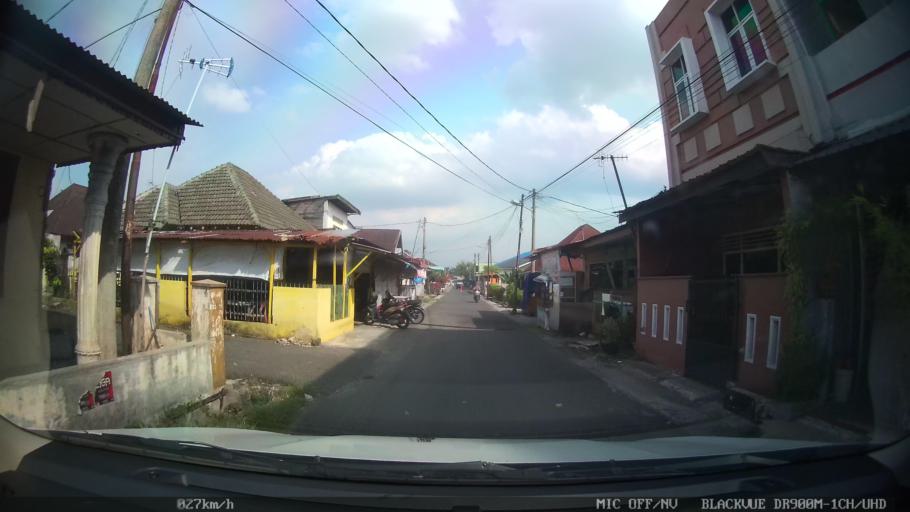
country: ID
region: North Sumatra
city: Binjai
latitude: 3.6154
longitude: 98.4977
